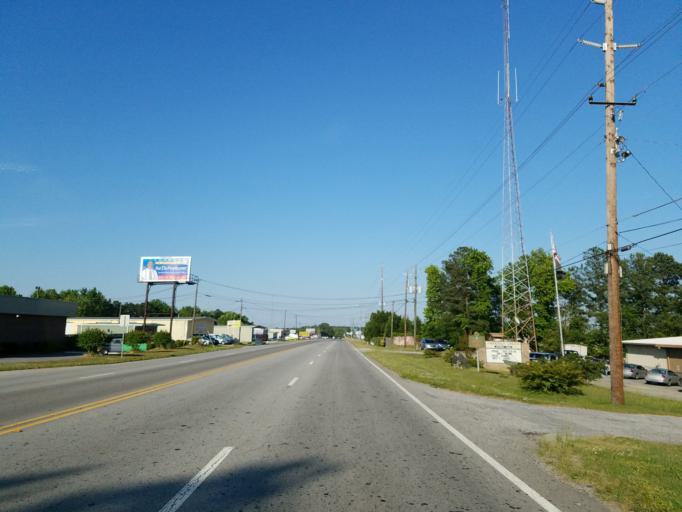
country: US
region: Georgia
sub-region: Douglas County
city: Douglasville
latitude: 33.7400
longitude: -84.7861
